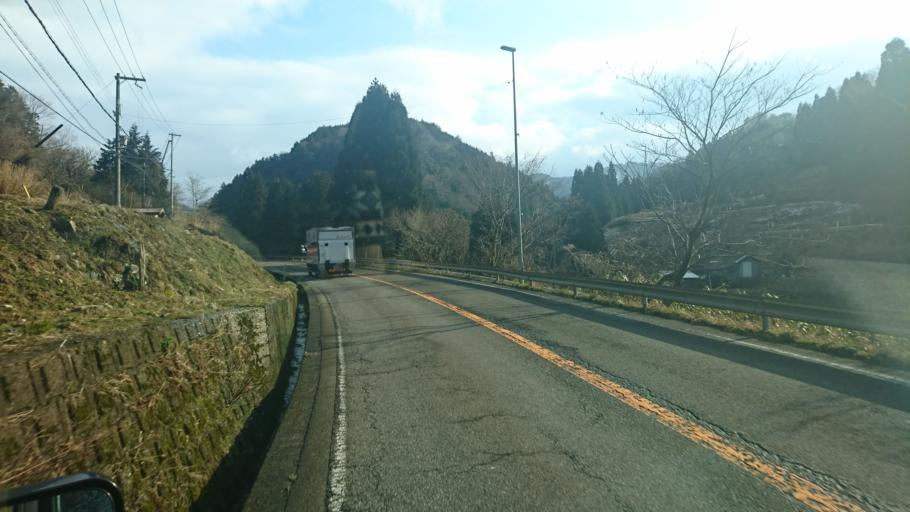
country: JP
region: Tottori
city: Tottori
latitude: 35.5374
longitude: 134.5112
